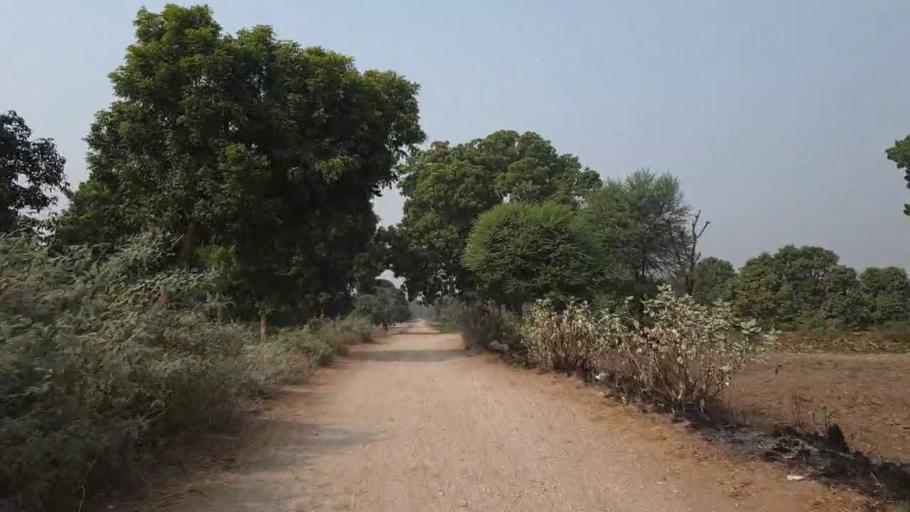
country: PK
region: Sindh
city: Tando Muhammad Khan
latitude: 25.2214
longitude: 68.5523
